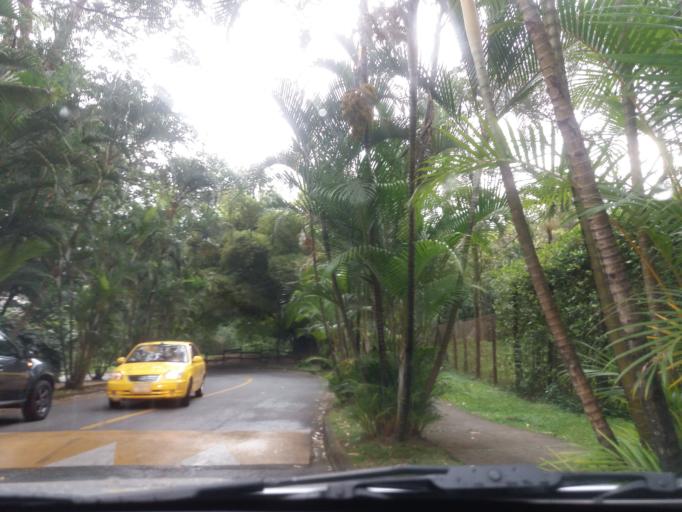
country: CO
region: Antioquia
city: Envigado
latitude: 6.2049
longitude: -75.5659
